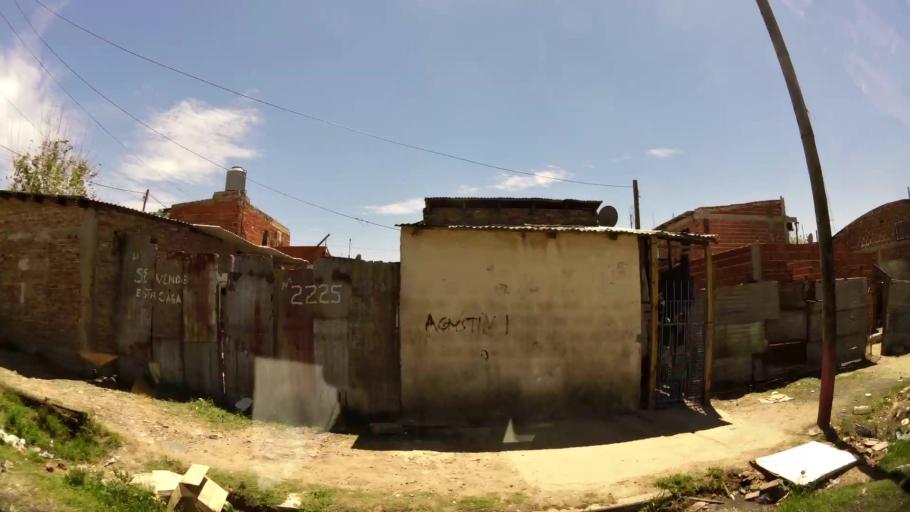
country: AR
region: Buenos Aires
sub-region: Partido de Quilmes
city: Quilmes
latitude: -34.7246
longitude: -58.3241
